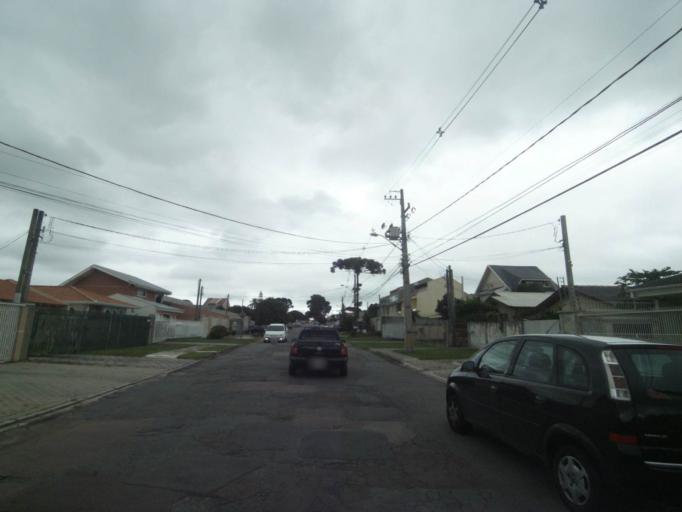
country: BR
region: Parana
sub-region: Curitiba
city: Curitiba
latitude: -25.4928
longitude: -49.2812
